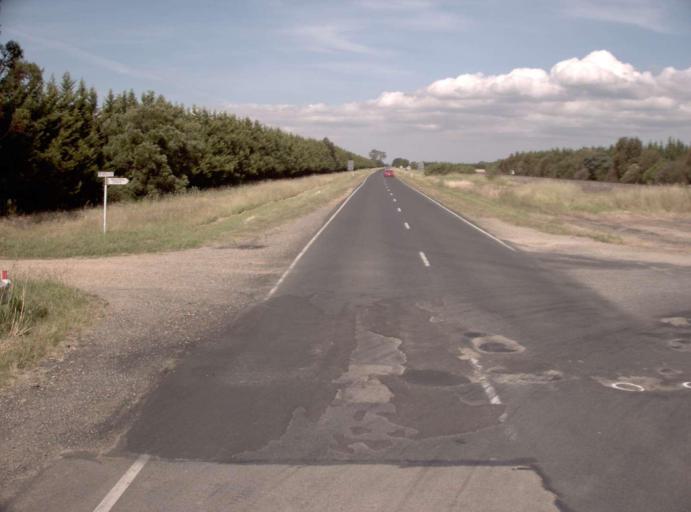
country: AU
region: Victoria
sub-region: Wellington
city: Heyfield
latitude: -38.1542
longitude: 146.7953
